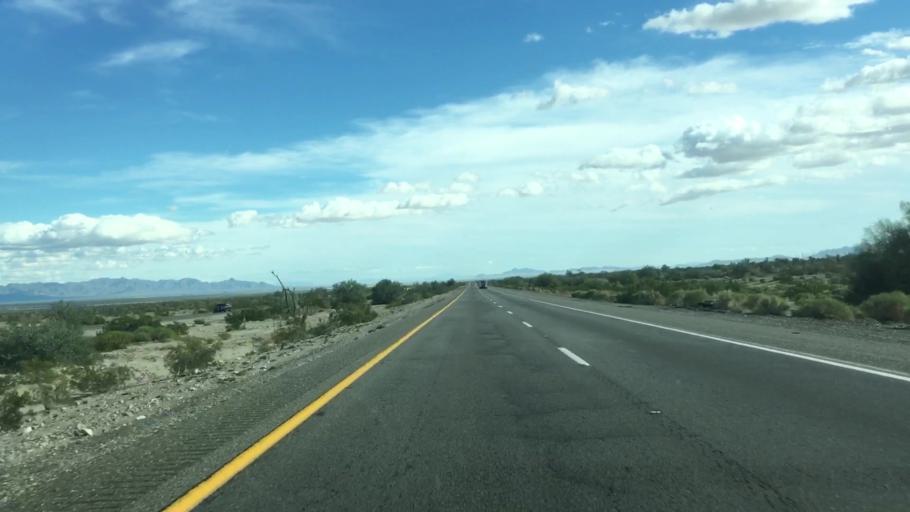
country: US
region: California
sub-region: Riverside County
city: Mesa Verde
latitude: 33.6762
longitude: -115.2230
